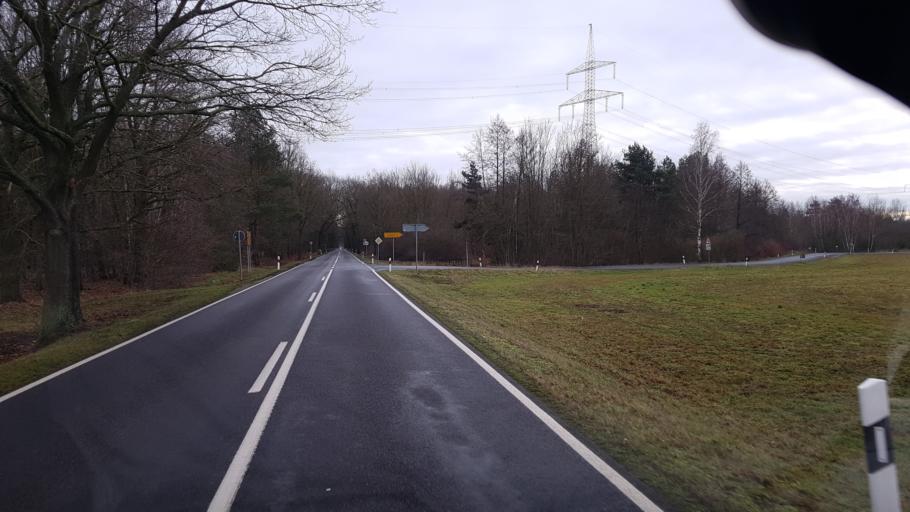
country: DE
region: Brandenburg
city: Altdobern
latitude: 51.6698
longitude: 14.0336
